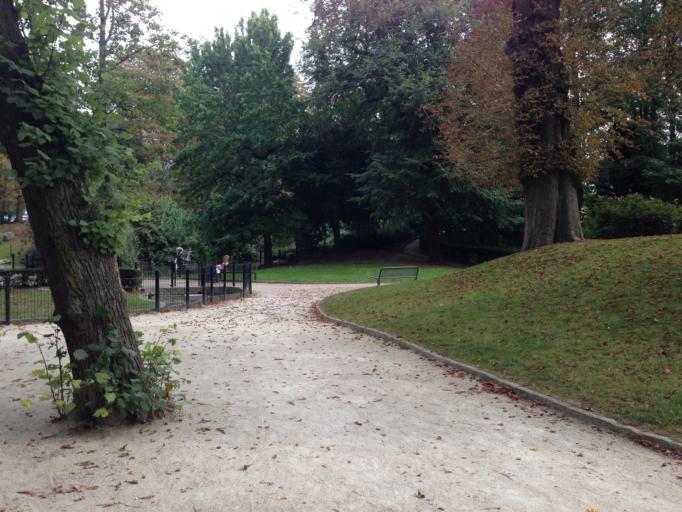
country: FR
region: Ile-de-France
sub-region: Departement du Val-de-Marne
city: Fontenay-sous-Bois
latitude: 48.8487
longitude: 2.4736
